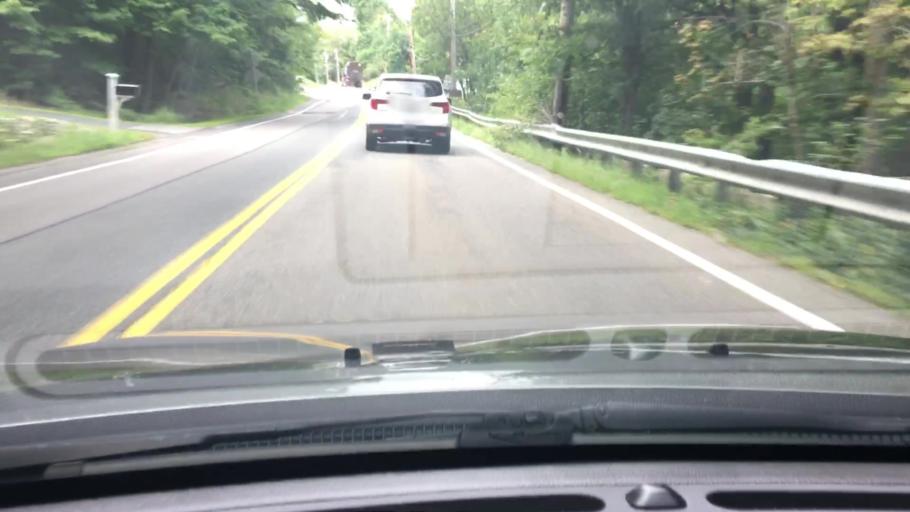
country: US
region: Massachusetts
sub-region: Middlesex County
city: Hopkinton
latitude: 42.2351
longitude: -71.5565
